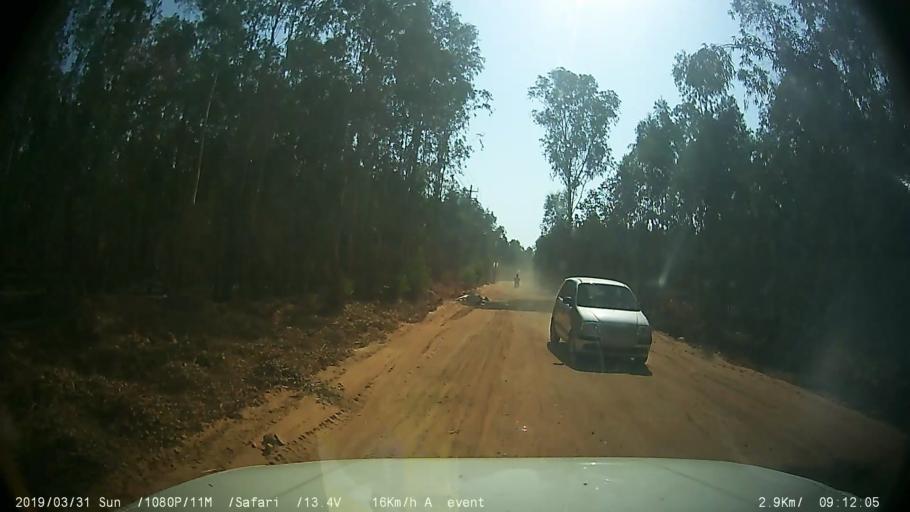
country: IN
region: Karnataka
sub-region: Bangalore Urban
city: Anekal
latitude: 12.8139
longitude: 77.6389
